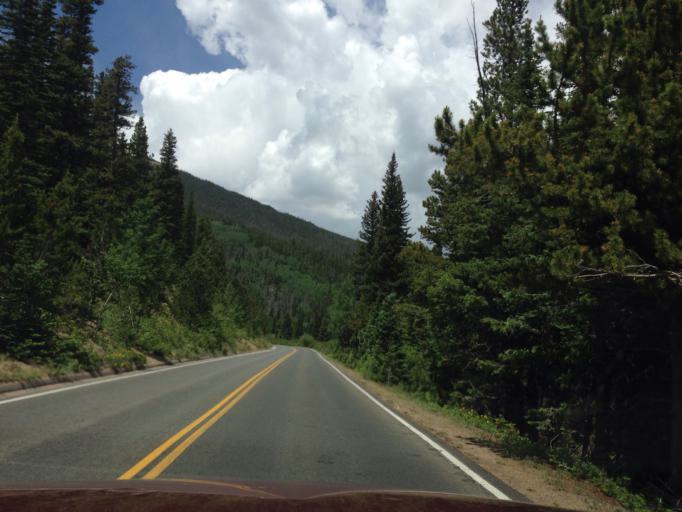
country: US
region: Colorado
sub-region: Larimer County
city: Estes Park
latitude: 40.3992
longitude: -105.6420
